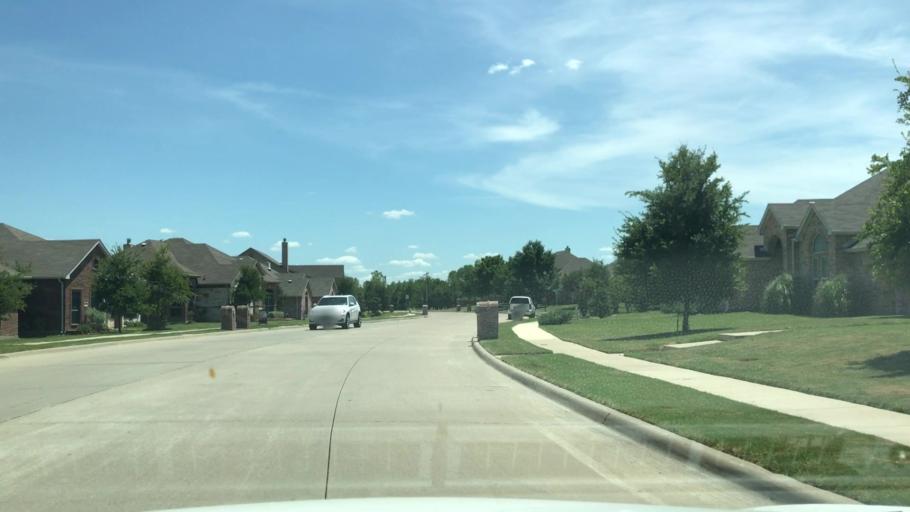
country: US
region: Texas
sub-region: Rockwall County
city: Rockwall
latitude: 32.8924
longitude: -96.4557
